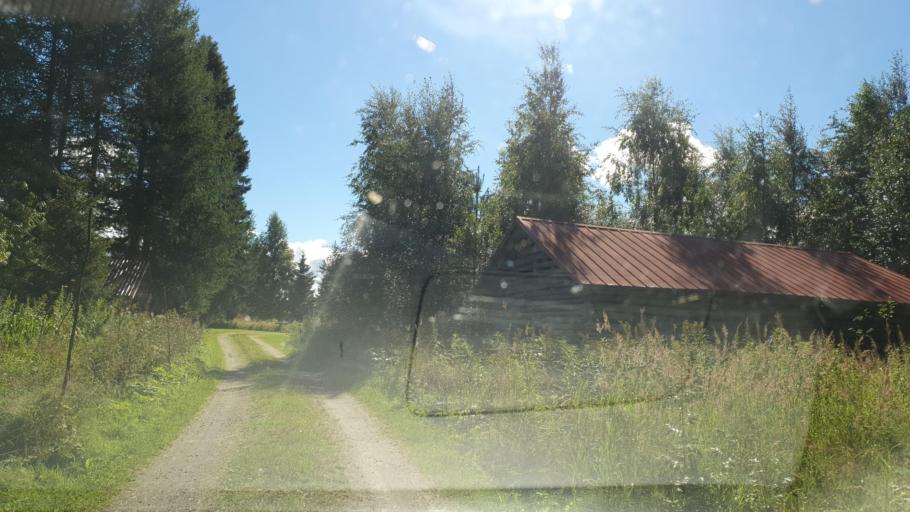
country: FI
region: Kainuu
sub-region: Kehys-Kainuu
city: Kuhmo
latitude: 64.1273
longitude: 29.3962
